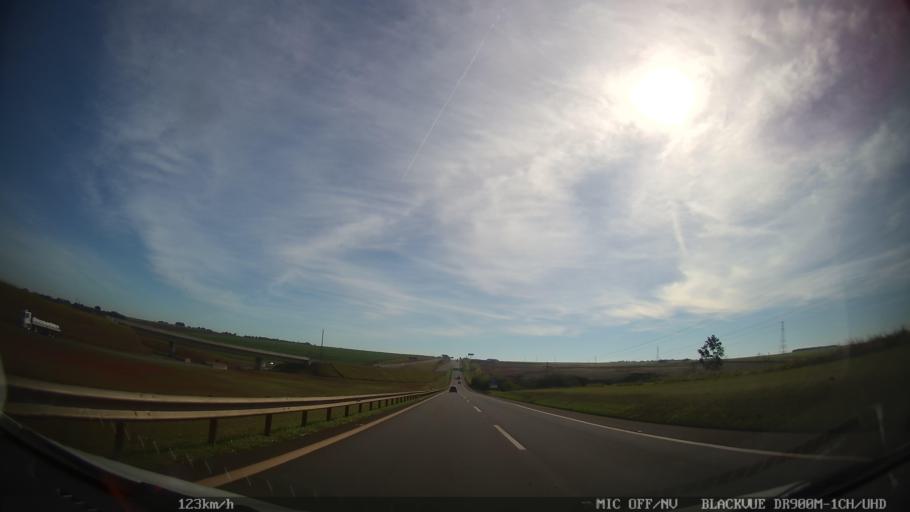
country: BR
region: Sao Paulo
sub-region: Cordeiropolis
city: Cordeiropolis
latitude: -22.4833
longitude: -47.3991
